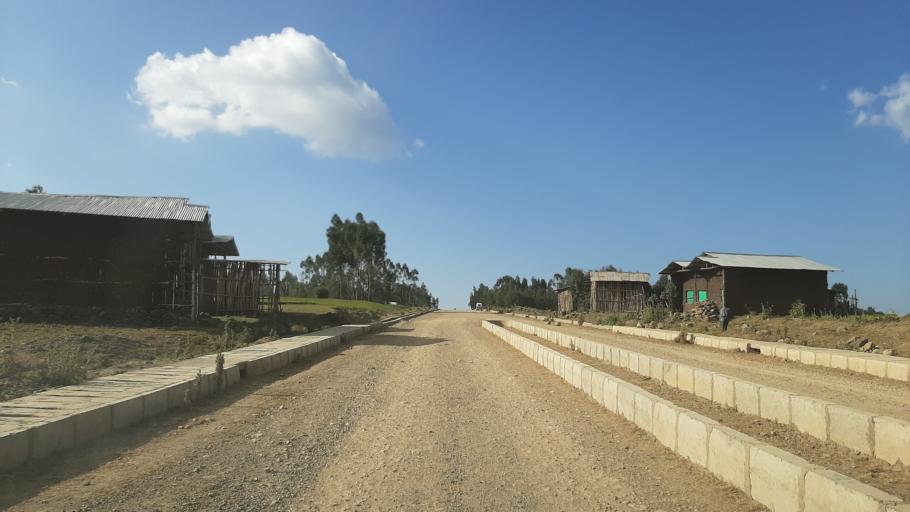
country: ET
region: Amhara
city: Dabat
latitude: 12.9959
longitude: 37.7638
